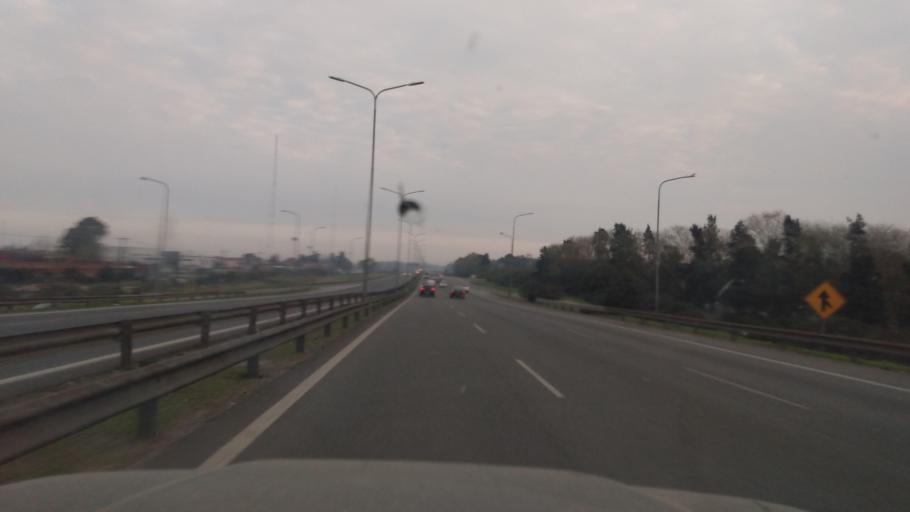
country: AR
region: Buenos Aires
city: Hurlingham
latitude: -34.5339
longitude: -58.5968
